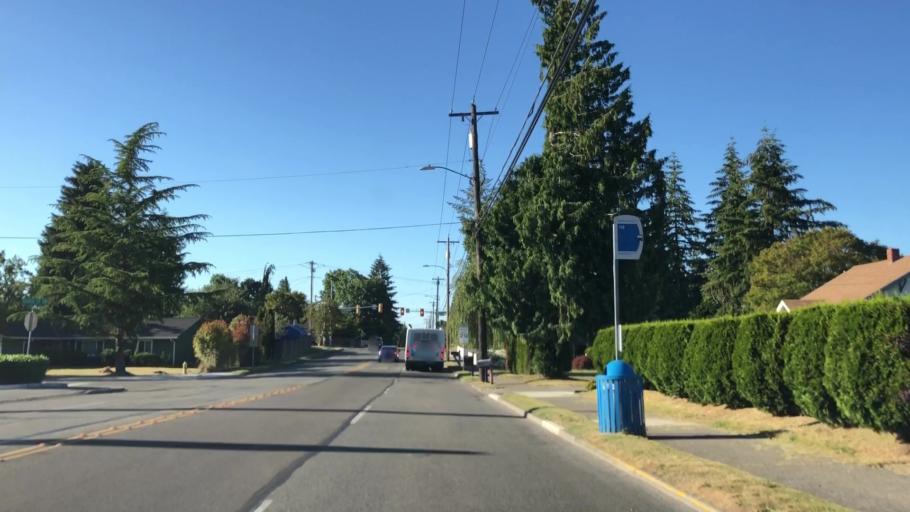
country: US
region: Washington
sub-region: Snohomish County
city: Mountlake Terrace
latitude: 47.7958
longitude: -122.2923
